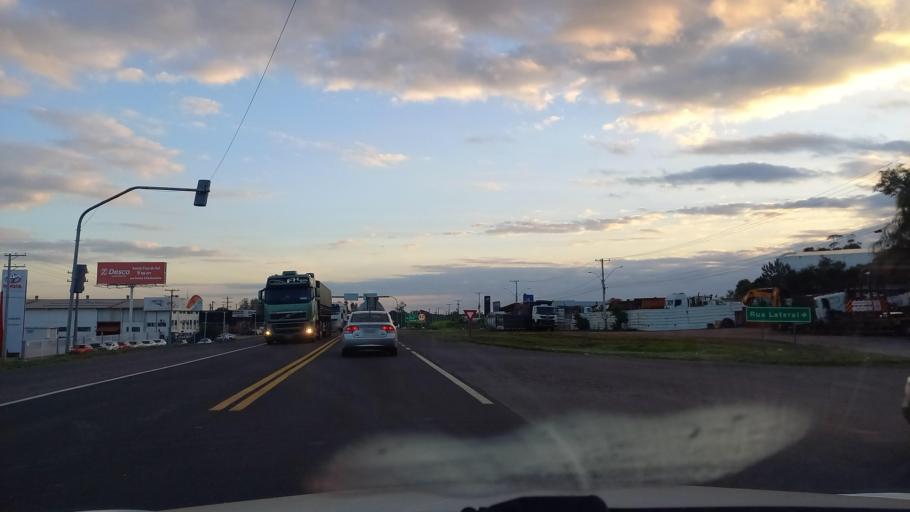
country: BR
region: Rio Grande do Sul
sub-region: Santa Cruz Do Sul
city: Santa Cruz do Sul
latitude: -29.6868
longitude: -52.4460
